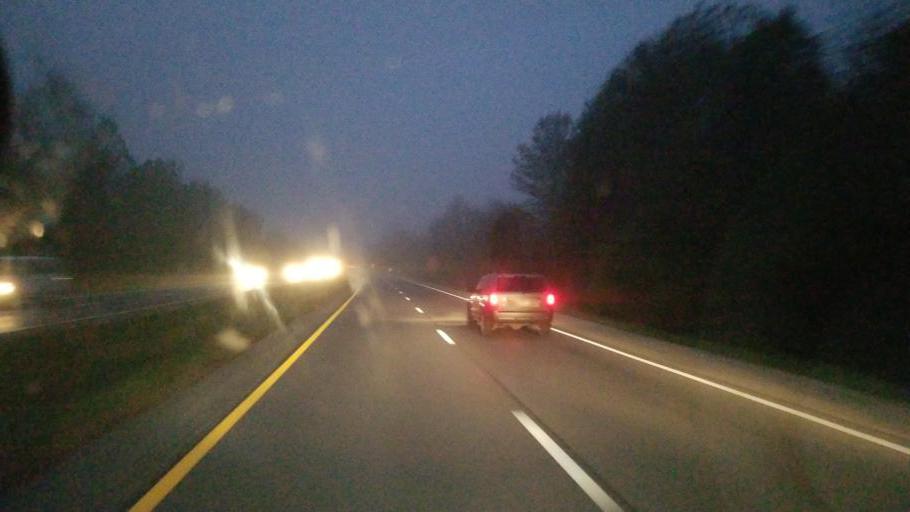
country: US
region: Ohio
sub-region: Ross County
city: Chillicothe
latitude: 39.2744
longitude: -82.9618
